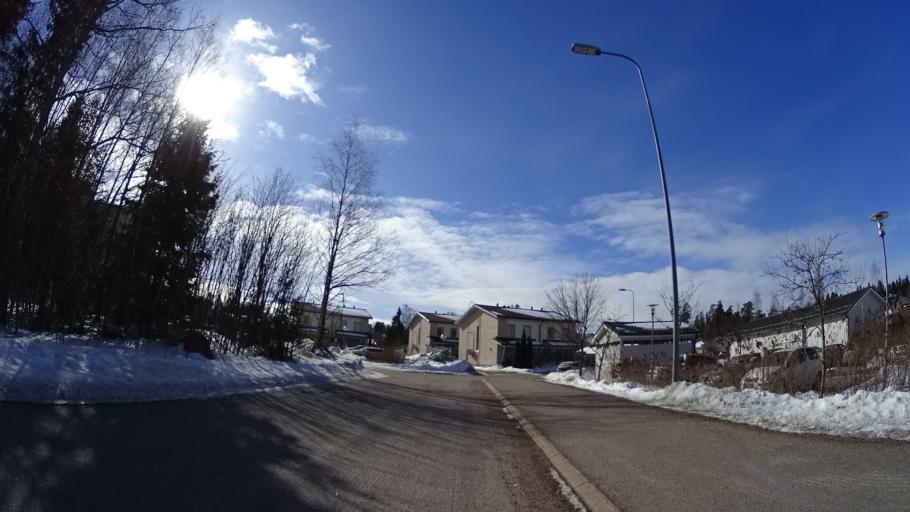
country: FI
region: Uusimaa
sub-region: Helsinki
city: Kauniainen
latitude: 60.2259
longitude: 24.6985
